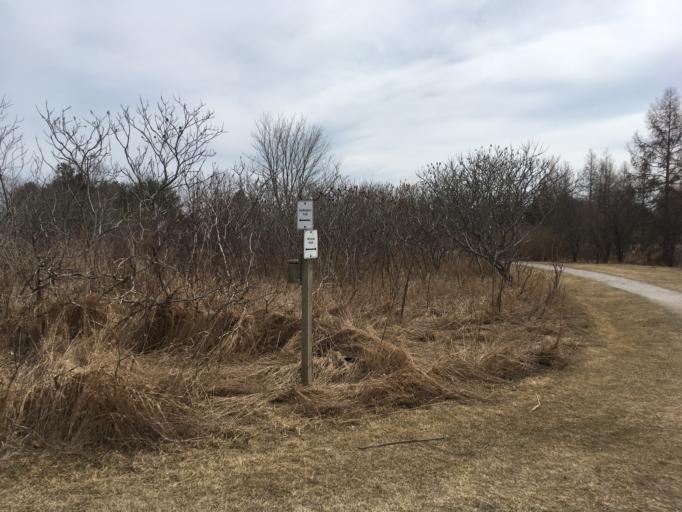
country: CA
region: Ontario
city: Oshawa
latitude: 43.8740
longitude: -78.8032
